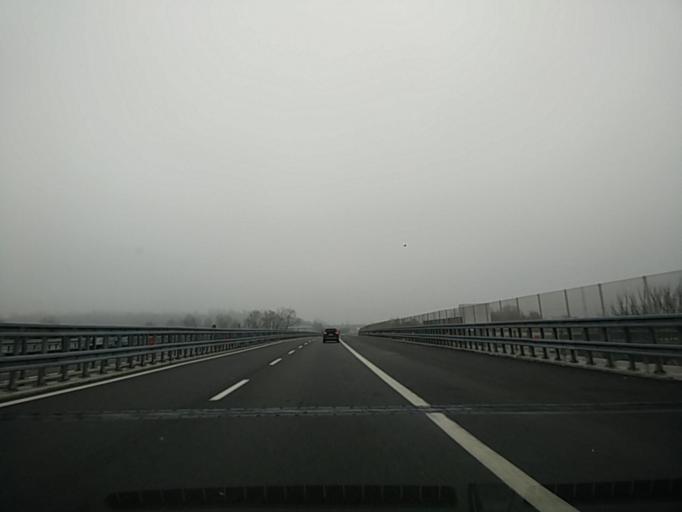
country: IT
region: Piedmont
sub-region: Provincia di Asti
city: Asti
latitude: 44.9136
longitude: 8.2284
